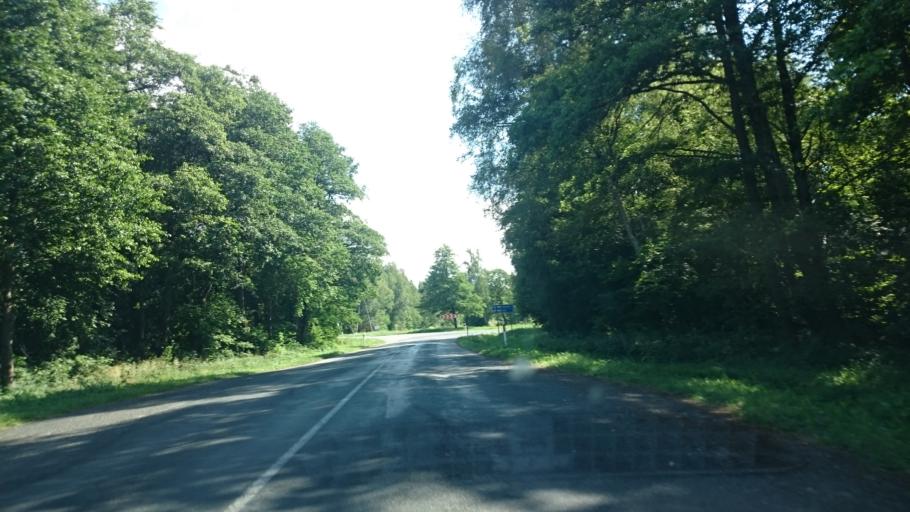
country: EE
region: Saare
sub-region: Orissaare vald
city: Orissaare
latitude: 58.5700
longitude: 22.7611
